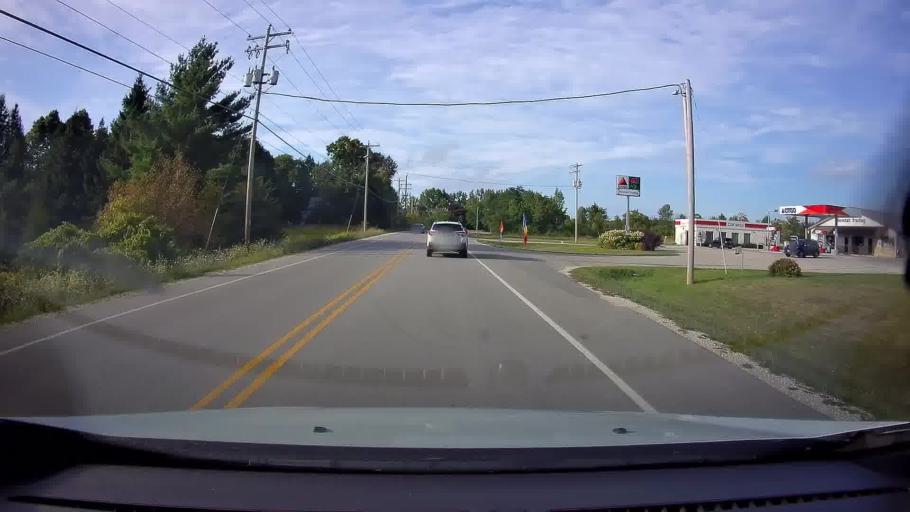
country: US
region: Wisconsin
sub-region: Door County
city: Sturgeon Bay
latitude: 45.1686
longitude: -87.1325
